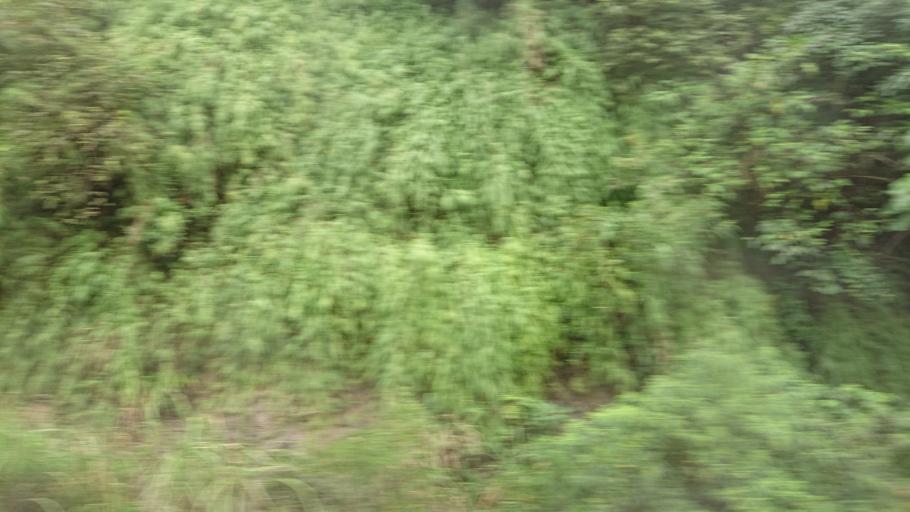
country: TW
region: Taiwan
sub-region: Keelung
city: Keelung
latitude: 25.1002
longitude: 121.7239
